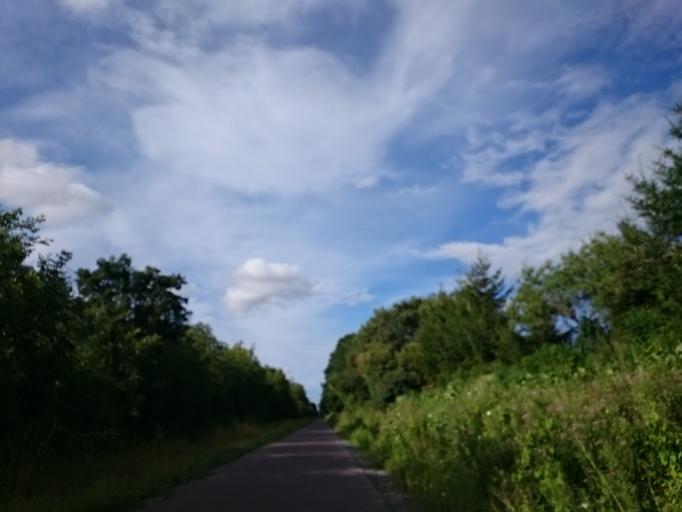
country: FR
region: Lower Normandy
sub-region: Departement du Calvados
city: Saint-Andre-sur-Orne
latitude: 49.1328
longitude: -0.4004
